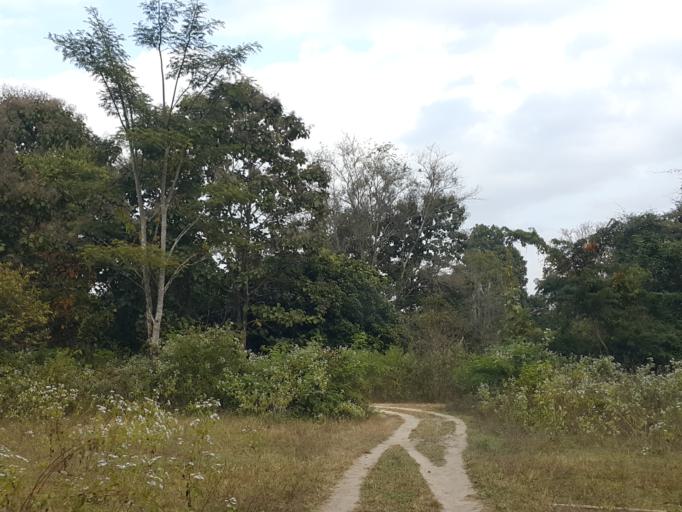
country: TH
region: Chiang Mai
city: Om Koi
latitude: 17.7968
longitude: 98.3415
